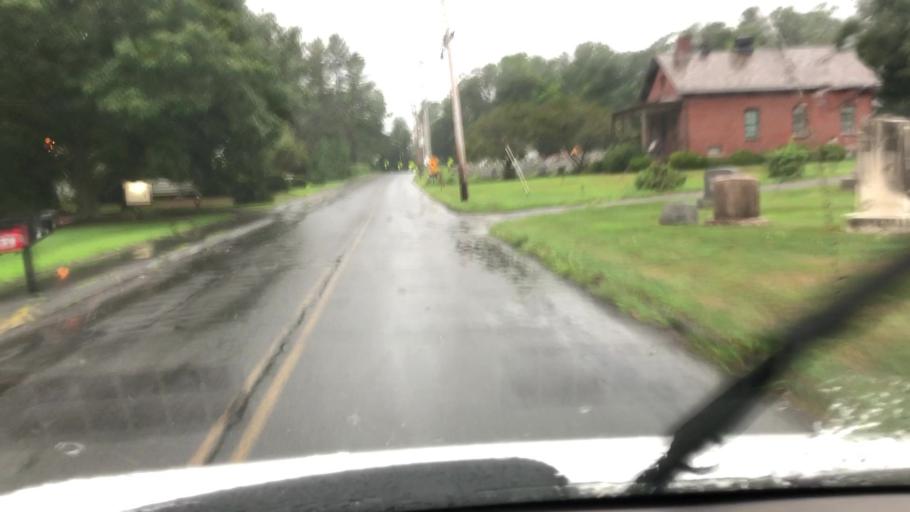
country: US
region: Massachusetts
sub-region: Hampshire County
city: Northampton
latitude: 42.3362
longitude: -72.6521
